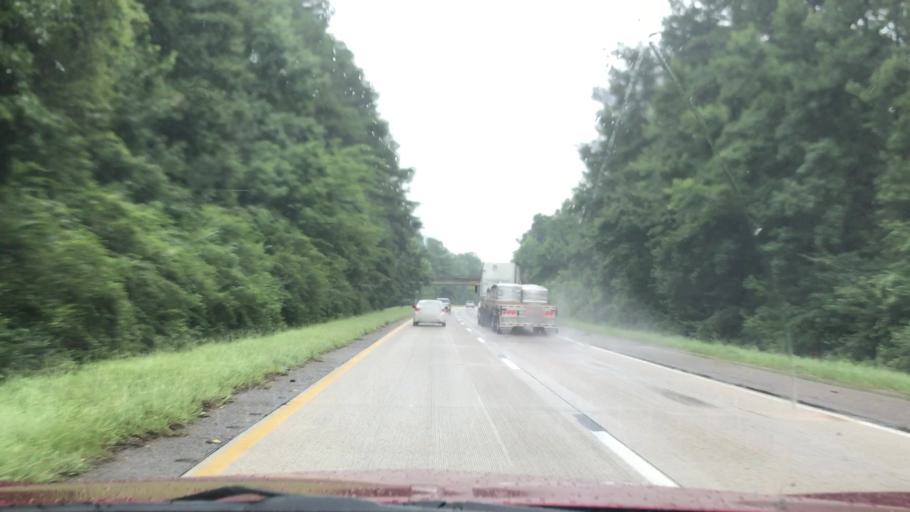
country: US
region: South Carolina
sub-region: Orangeburg County
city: Holly Hill
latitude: 33.2243
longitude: -80.4276
